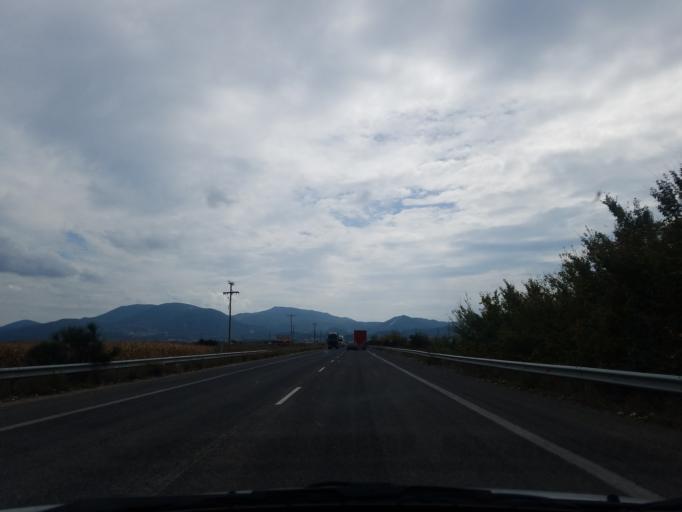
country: GR
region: Central Greece
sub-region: Nomos Fthiotidos
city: Domokos
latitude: 39.0508
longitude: 22.3432
